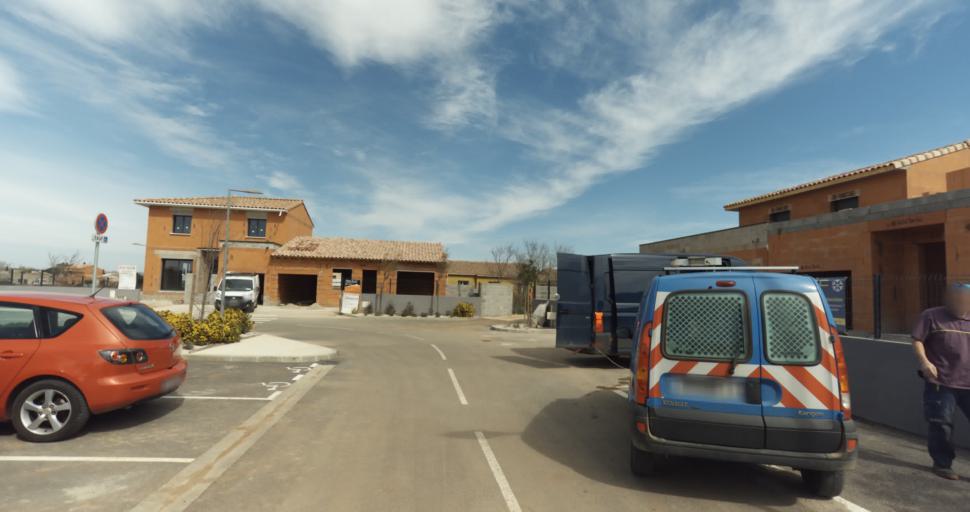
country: FR
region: Languedoc-Roussillon
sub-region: Departement de l'Herault
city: Marseillan
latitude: 43.3392
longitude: 3.5303
